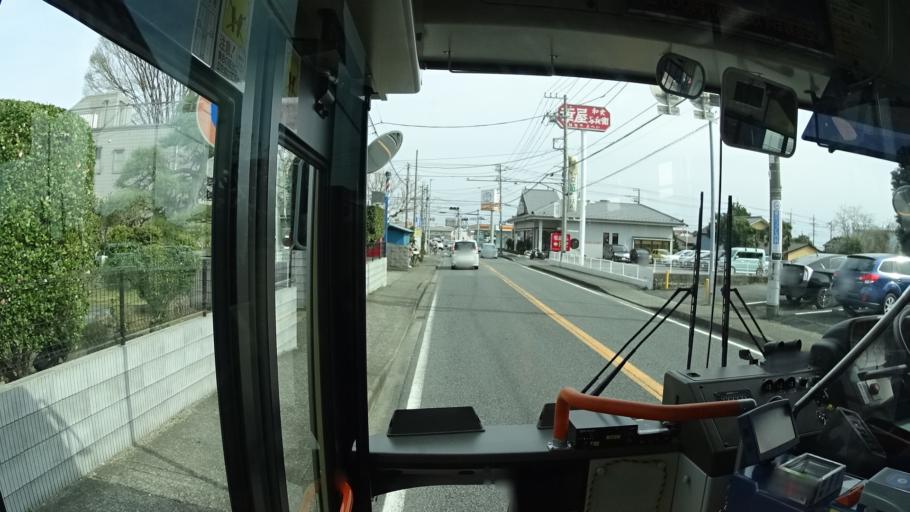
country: JP
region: Kanagawa
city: Atsugi
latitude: 35.4789
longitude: 139.3406
